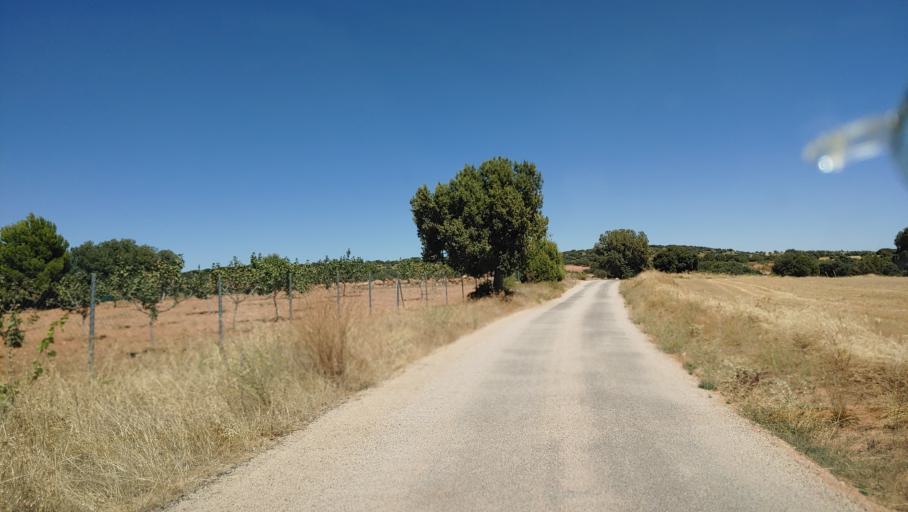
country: ES
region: Castille-La Mancha
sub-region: Provincia de Albacete
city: Ossa de Montiel
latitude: 38.9285
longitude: -2.7820
